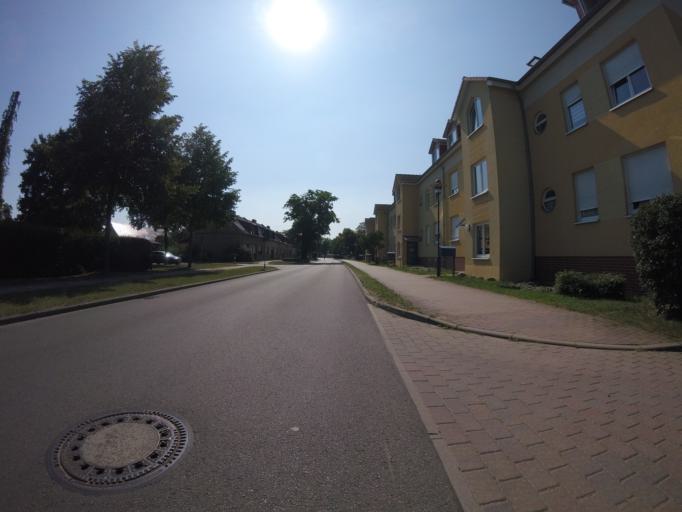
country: DE
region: Brandenburg
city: Mullrose
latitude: 52.2432
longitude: 14.4112
